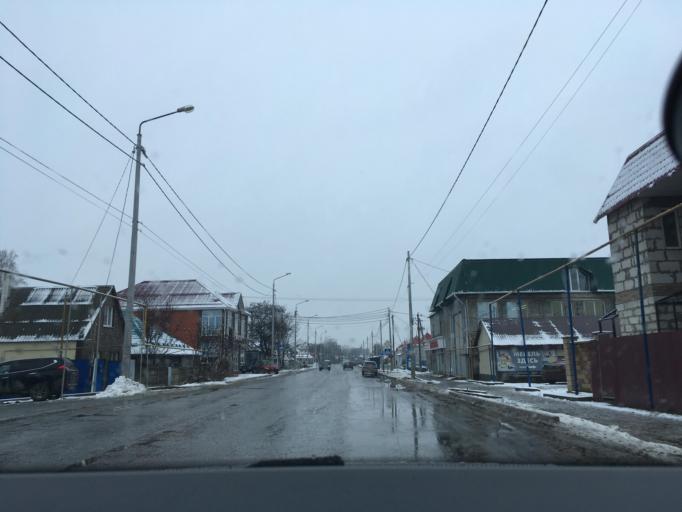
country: RU
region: Belgorod
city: Valuyki
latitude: 50.2023
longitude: 38.1155
